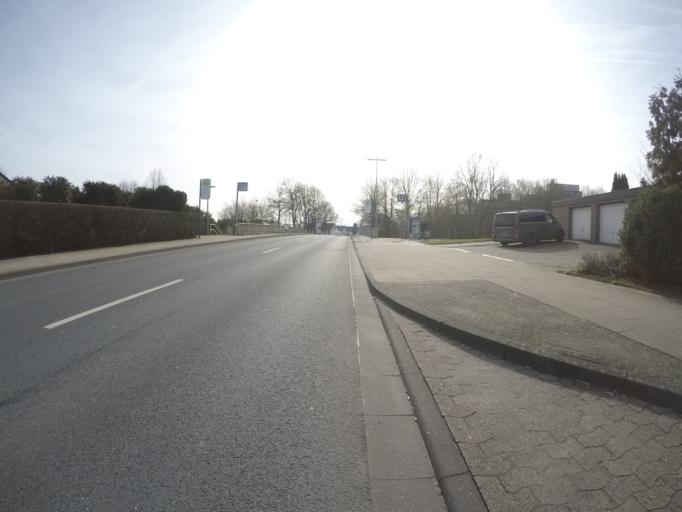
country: DE
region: North Rhine-Westphalia
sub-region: Regierungsbezirk Detmold
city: Bielefeld
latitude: 52.0536
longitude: 8.6026
